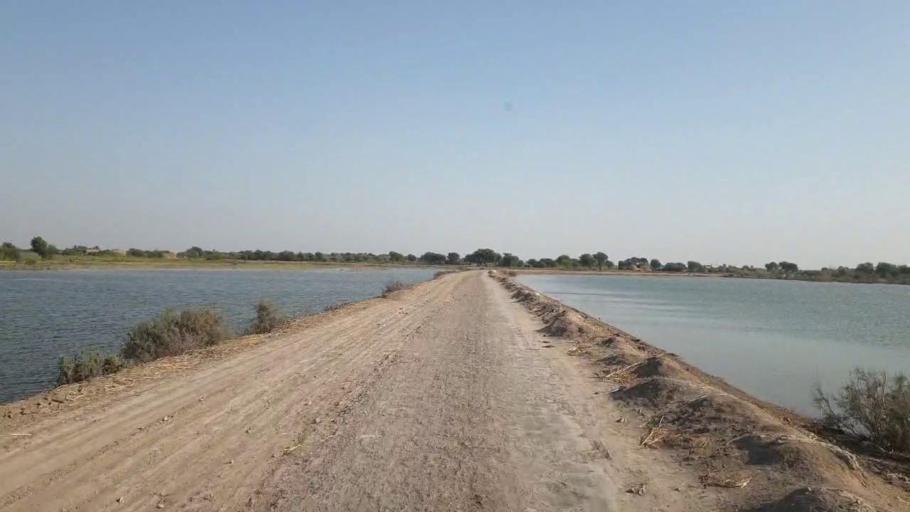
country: PK
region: Sindh
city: Matli
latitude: 25.0073
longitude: 68.7426
